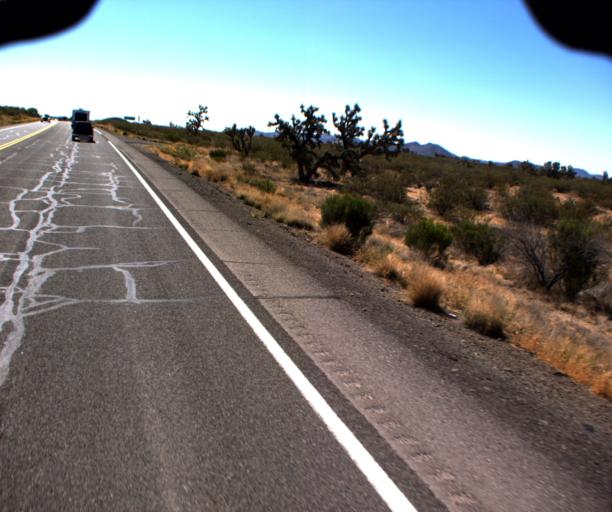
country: US
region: Arizona
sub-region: Yavapai County
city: Congress
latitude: 34.1863
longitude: -113.0468
